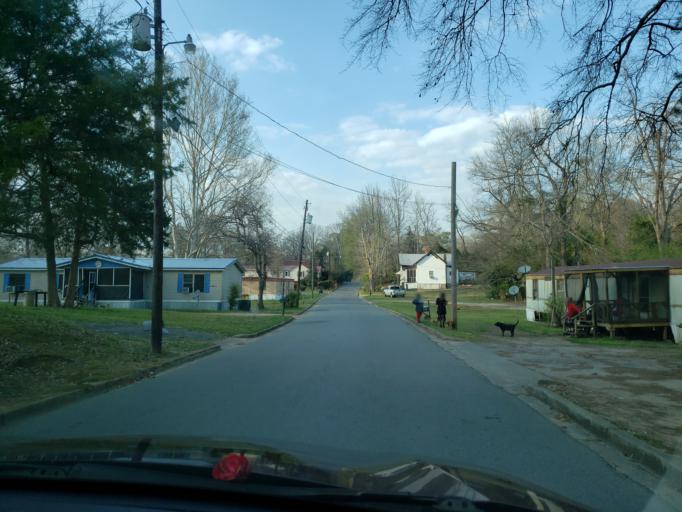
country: US
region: Alabama
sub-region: Hale County
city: Greensboro
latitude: 32.7065
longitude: -87.5991
